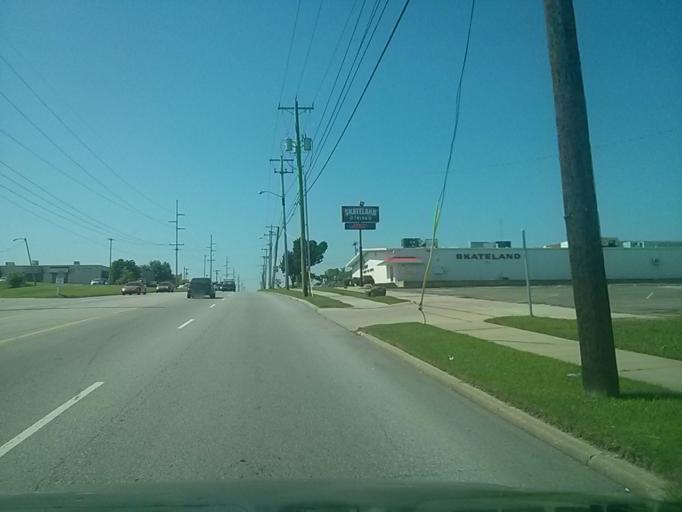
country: US
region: Oklahoma
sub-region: Tulsa County
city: Tulsa
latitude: 36.1473
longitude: -95.9047
